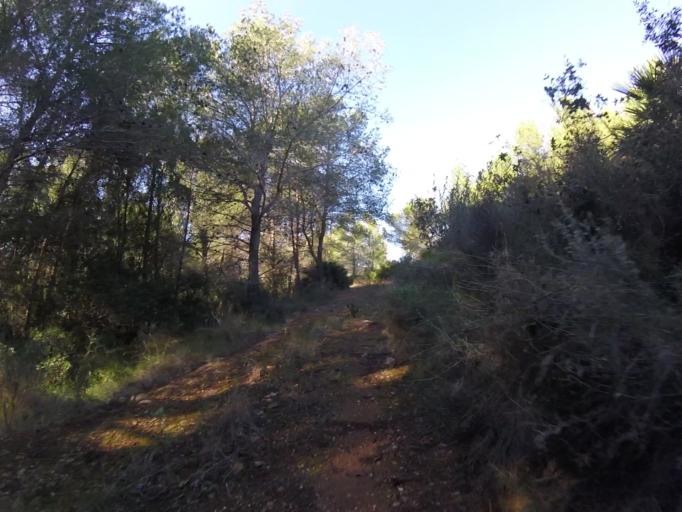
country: ES
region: Valencia
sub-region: Provincia de Castello
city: Orpesa/Oropesa del Mar
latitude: 40.1217
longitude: 0.1193
